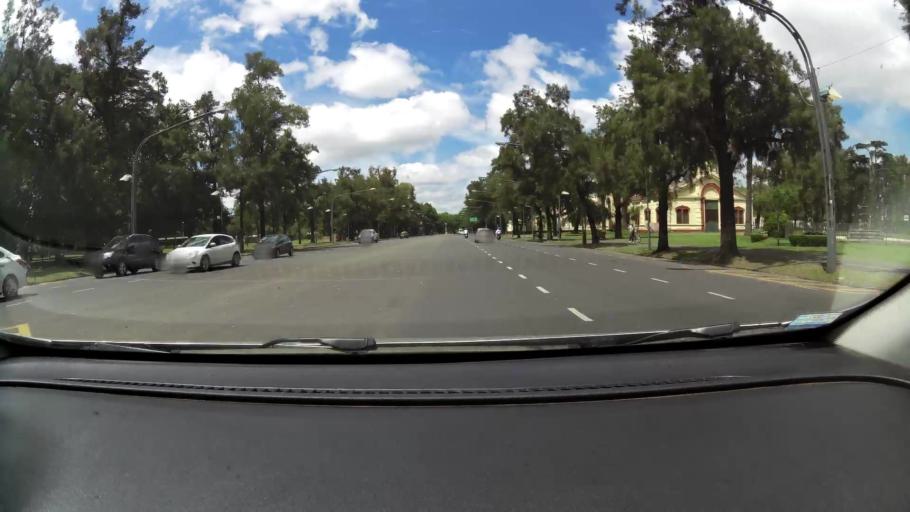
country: AR
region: Santa Fe
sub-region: Departamento de Rosario
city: Rosario
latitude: -32.9627
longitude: -60.6581
